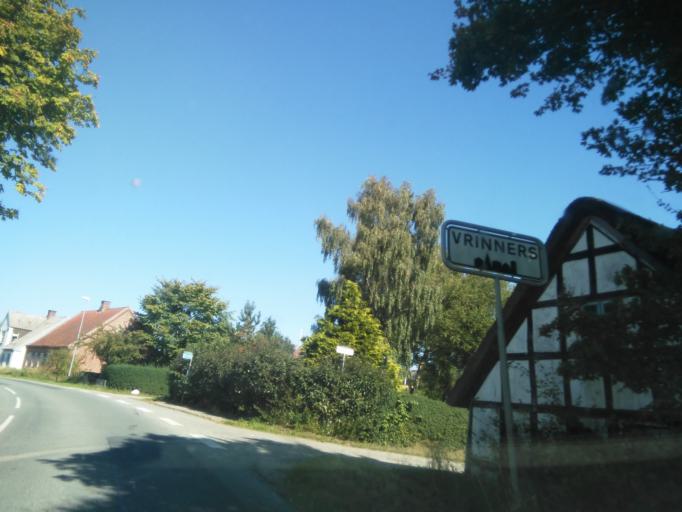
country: DK
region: Central Jutland
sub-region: Syddjurs Kommune
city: Ronde
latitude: 56.2388
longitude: 10.4931
